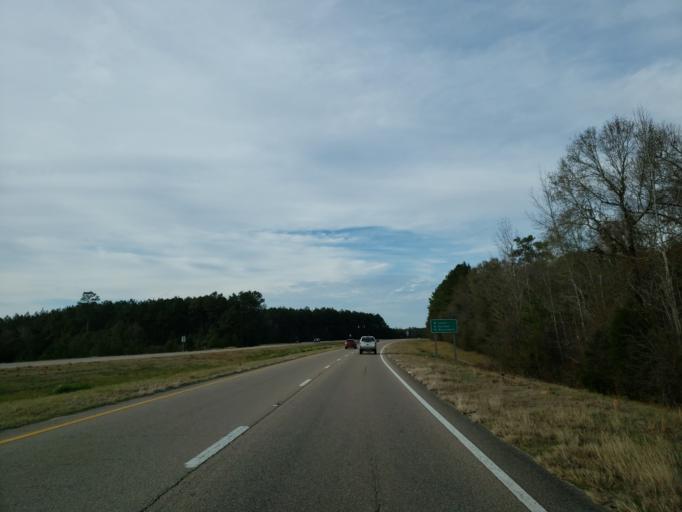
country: US
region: Mississippi
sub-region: Wayne County
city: Waynesboro
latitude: 31.6304
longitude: -88.5913
